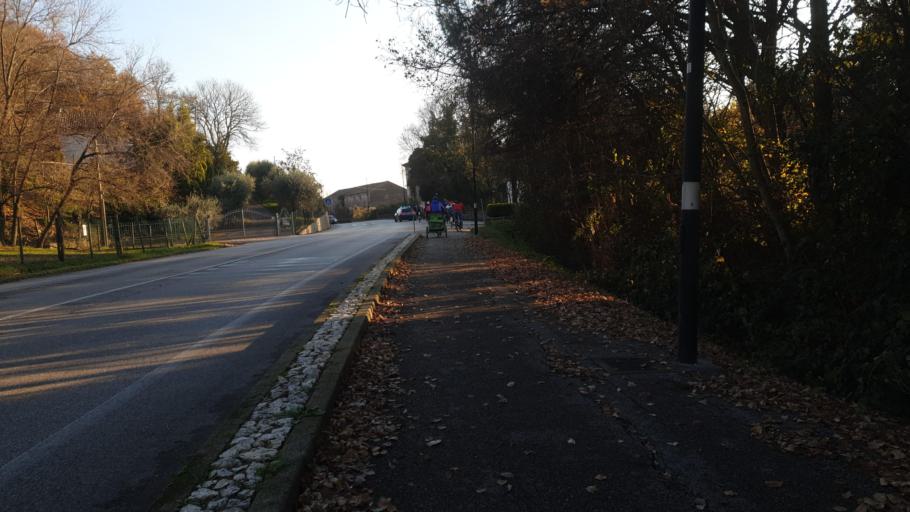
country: IT
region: Veneto
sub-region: Provincia di Padova
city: Battaglia Terme
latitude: 45.2932
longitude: 11.7689
